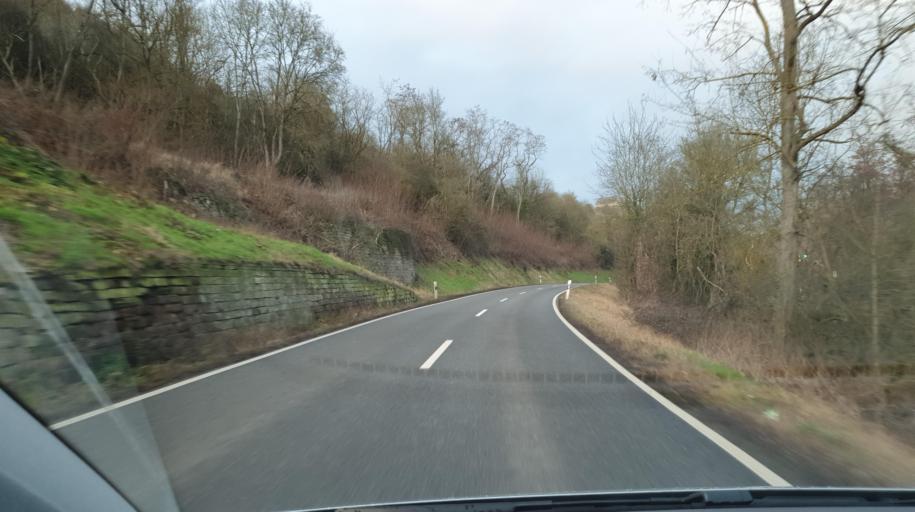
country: DE
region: Rheinland-Pfalz
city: Bad Munster am Stein-Ebernburg
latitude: 49.8007
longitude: 7.8331
